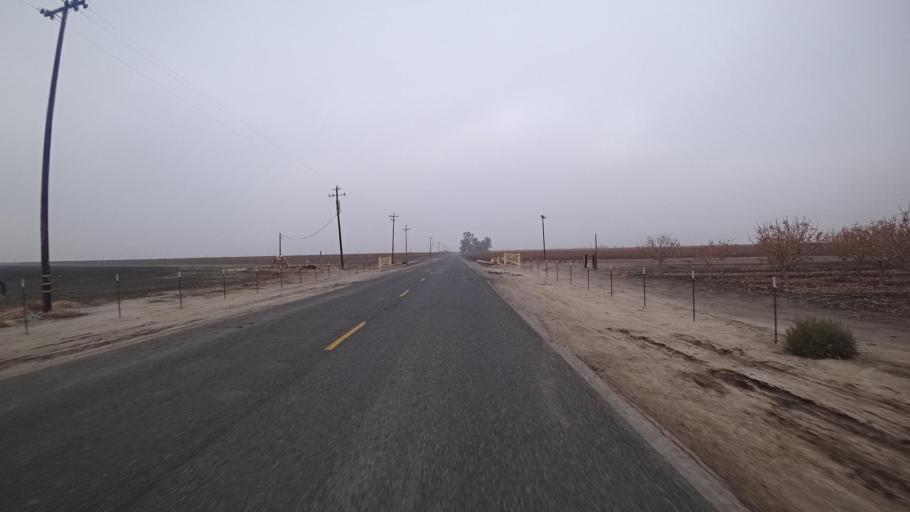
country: US
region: California
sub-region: Kern County
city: Buttonwillow
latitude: 35.3627
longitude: -119.4742
